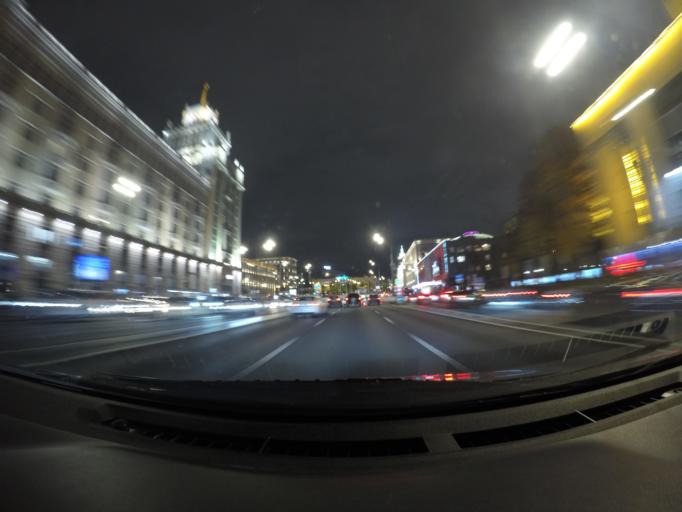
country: RU
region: Moscow
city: Moscow
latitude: 55.7678
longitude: 37.5936
